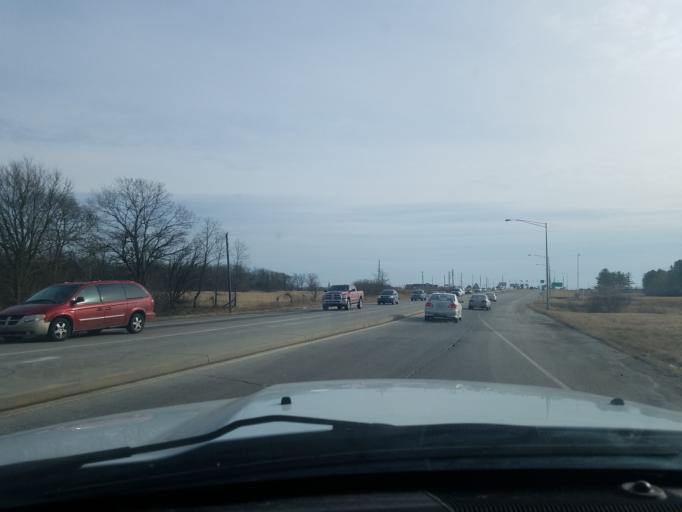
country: US
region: Indiana
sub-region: Hancock County
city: Greenfield
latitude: 39.8259
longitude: -85.7703
